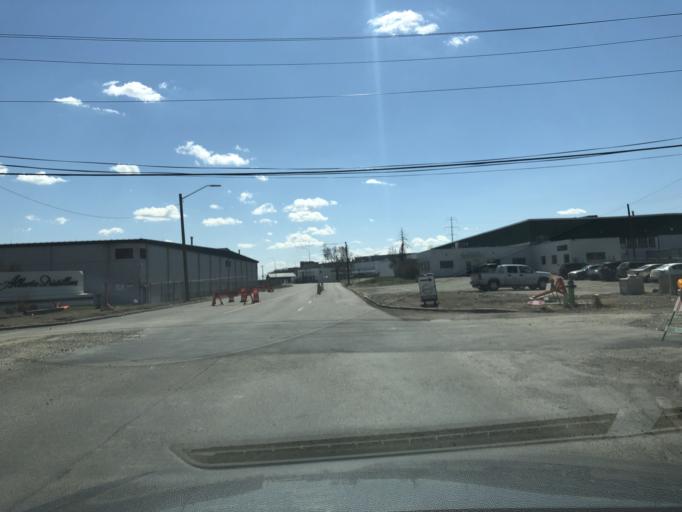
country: CA
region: Alberta
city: Calgary
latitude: 51.0234
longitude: -114.0310
